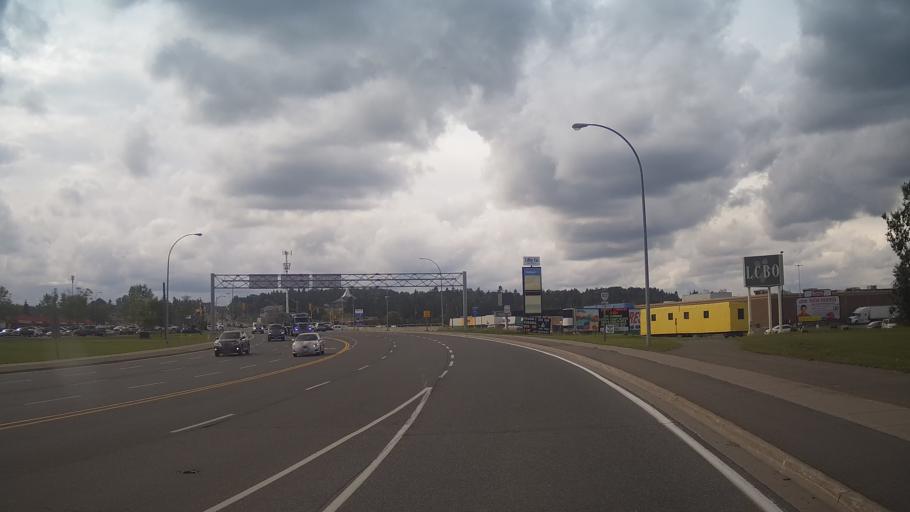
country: CA
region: Ontario
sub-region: Thunder Bay District
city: Thunder Bay
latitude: 48.4506
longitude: -89.2513
